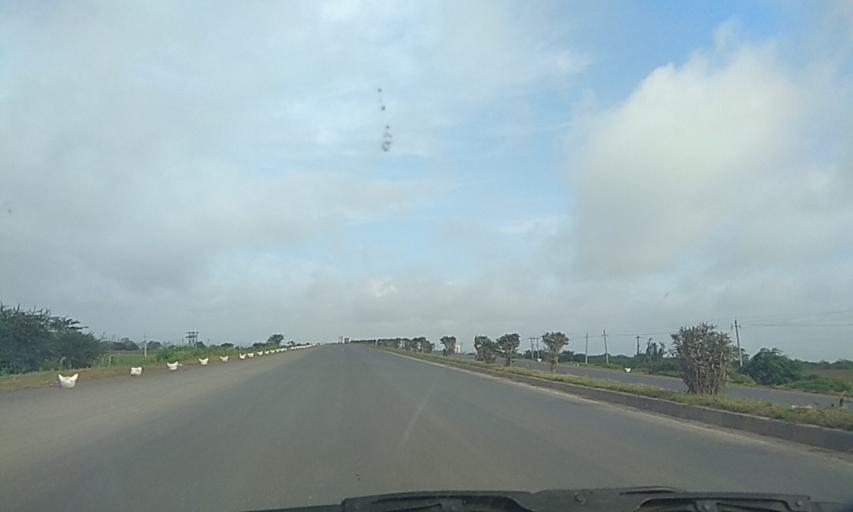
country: IN
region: Karnataka
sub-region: Haveri
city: Haveri
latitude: 14.8354
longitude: 75.3570
